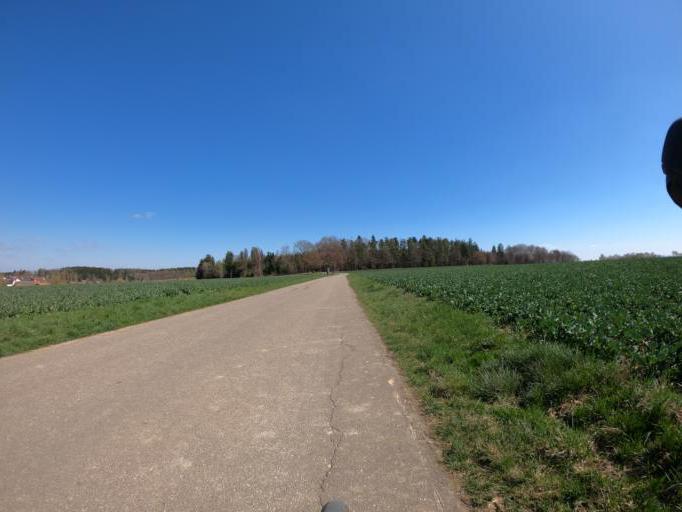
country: DE
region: Baden-Wuerttemberg
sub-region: Karlsruhe Region
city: Empfingen
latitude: 48.4063
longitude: 8.7305
